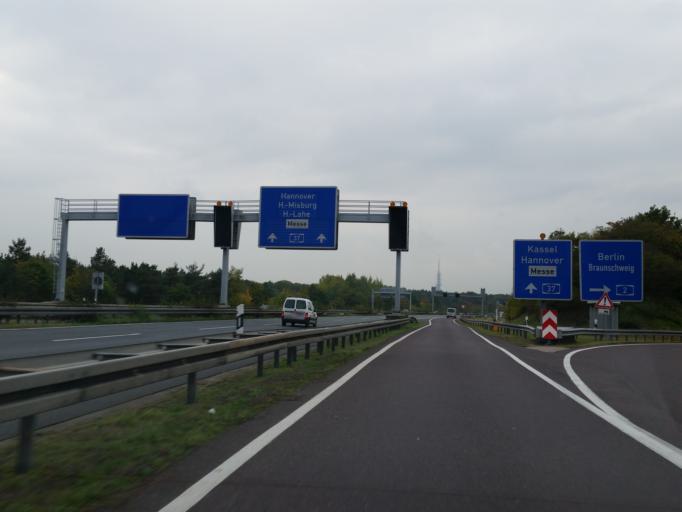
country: DE
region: Lower Saxony
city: Isernhagen Farster Bauerschaft
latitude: 52.4122
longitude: 9.8468
